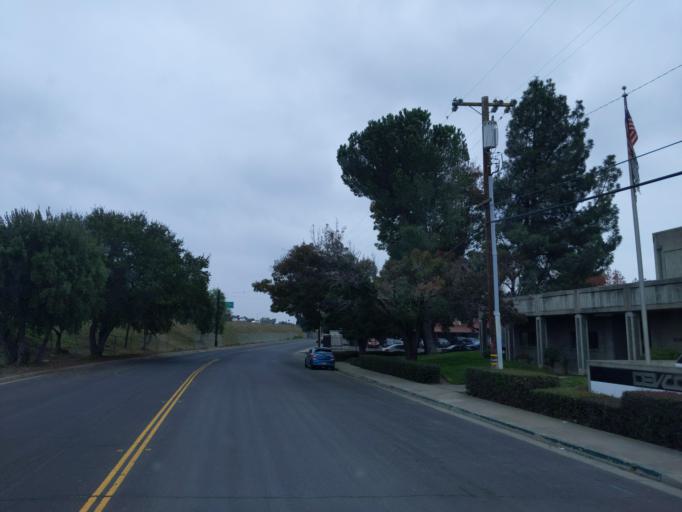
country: US
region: California
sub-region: San Joaquin County
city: Country Club
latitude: 37.9556
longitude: -121.3236
